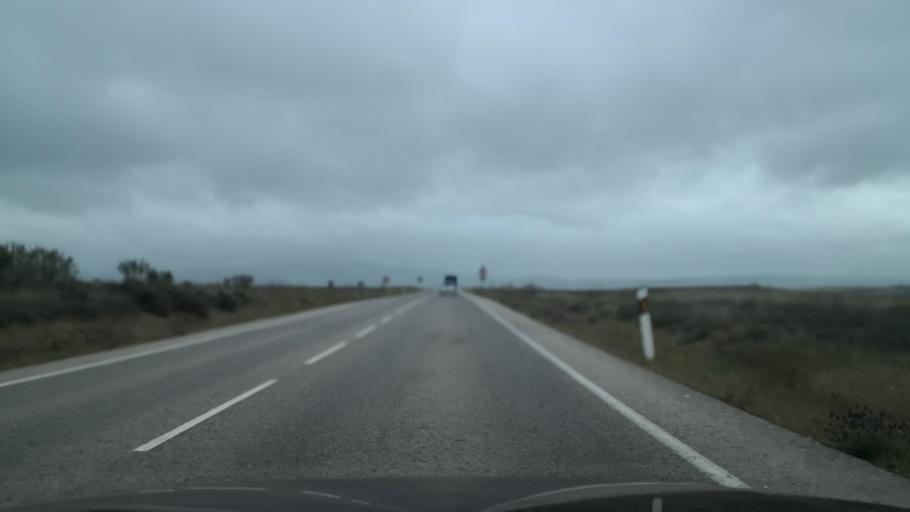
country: ES
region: Extremadura
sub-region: Provincia de Caceres
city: Malpartida de Caceres
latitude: 39.3499
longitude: -6.4700
